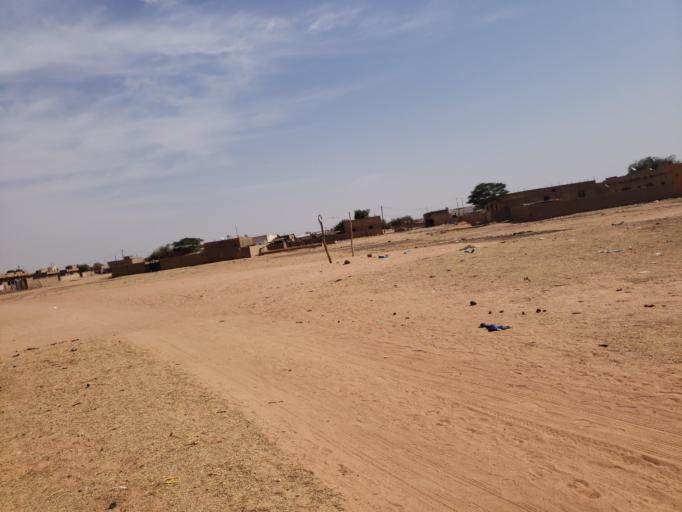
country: SN
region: Matam
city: Ranerou
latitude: 15.3010
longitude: -13.9617
